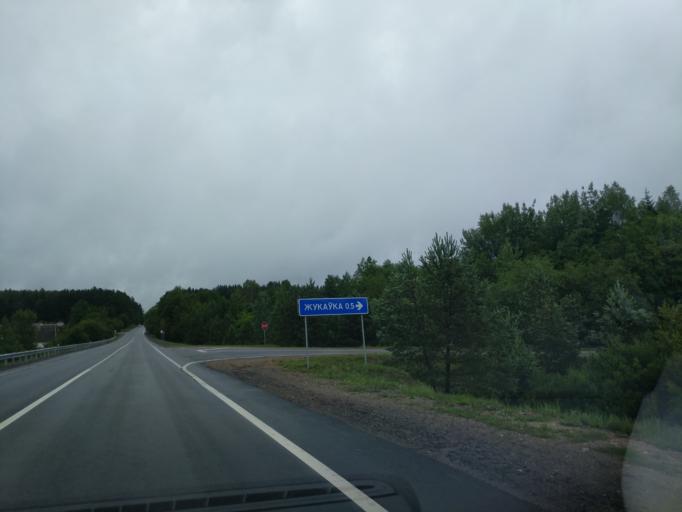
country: BY
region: Minsk
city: Syomkava
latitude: 54.1868
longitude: 27.5000
